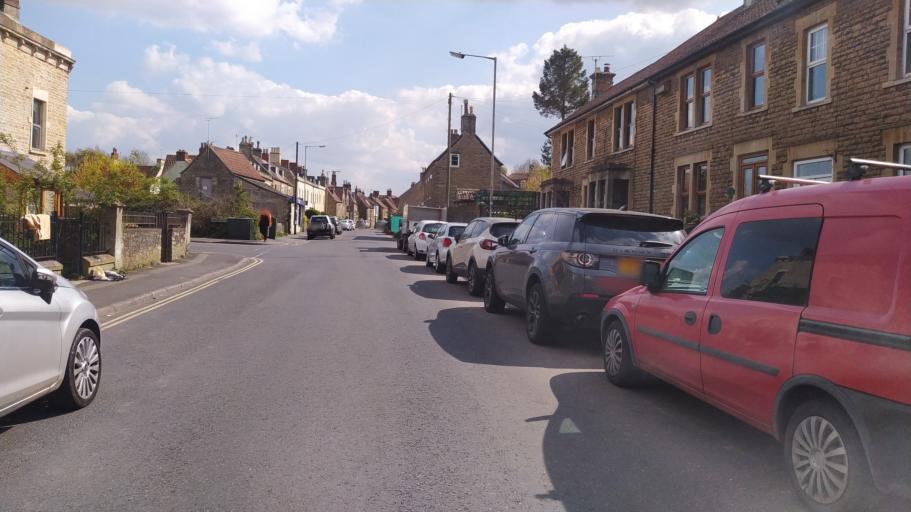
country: GB
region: England
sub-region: Somerset
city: Frome
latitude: 51.2268
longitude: -2.3221
